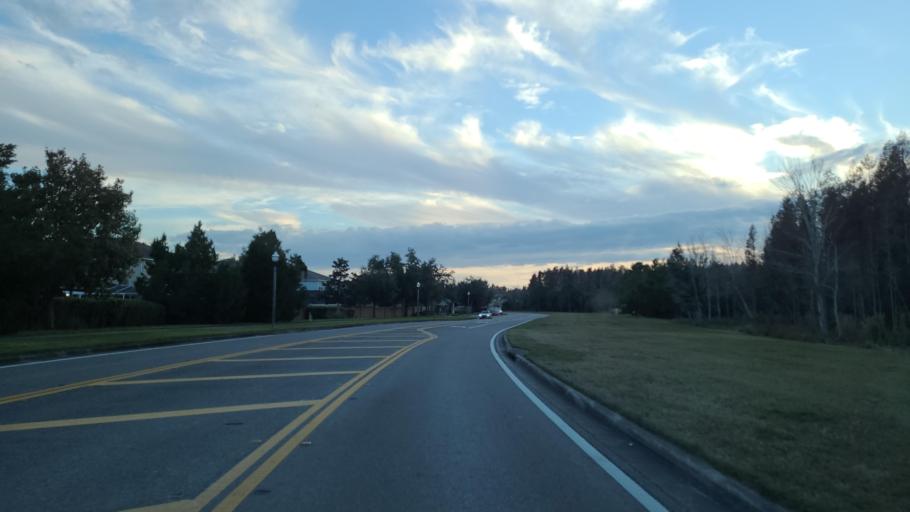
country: US
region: Florida
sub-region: Hillsborough County
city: Cheval
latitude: 28.2041
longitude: -82.5231
